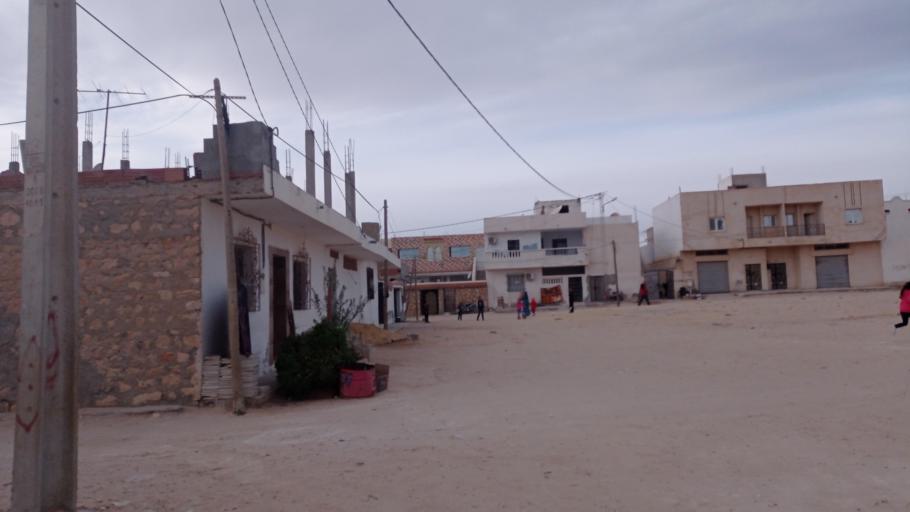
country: TN
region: Qabis
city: Gabes
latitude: 33.8376
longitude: 10.1143
